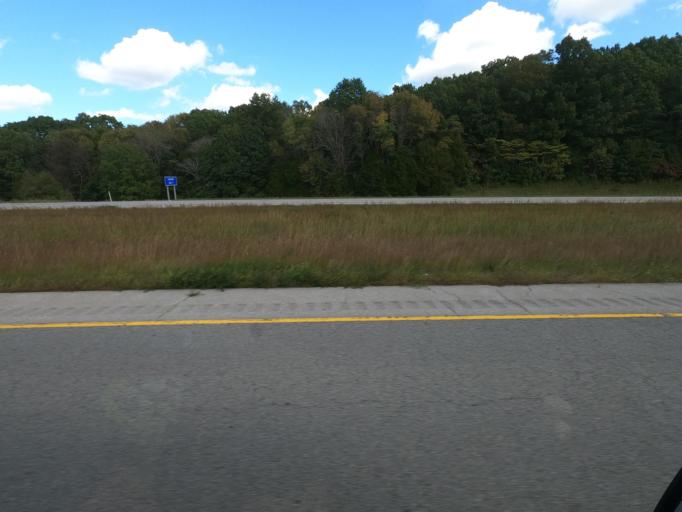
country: US
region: Illinois
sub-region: Johnson County
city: Goreville
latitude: 37.5191
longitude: -88.9131
